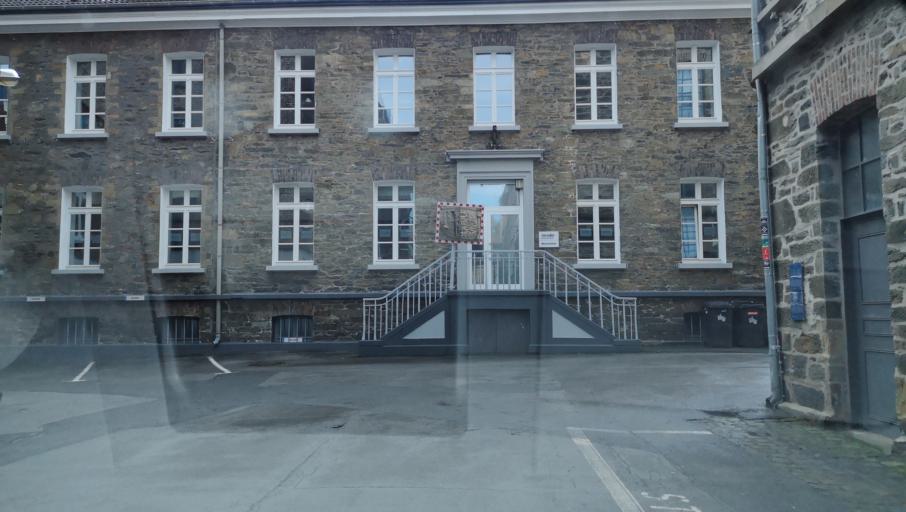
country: DE
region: North Rhine-Westphalia
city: Radevormwald
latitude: 51.2210
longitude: 7.3167
